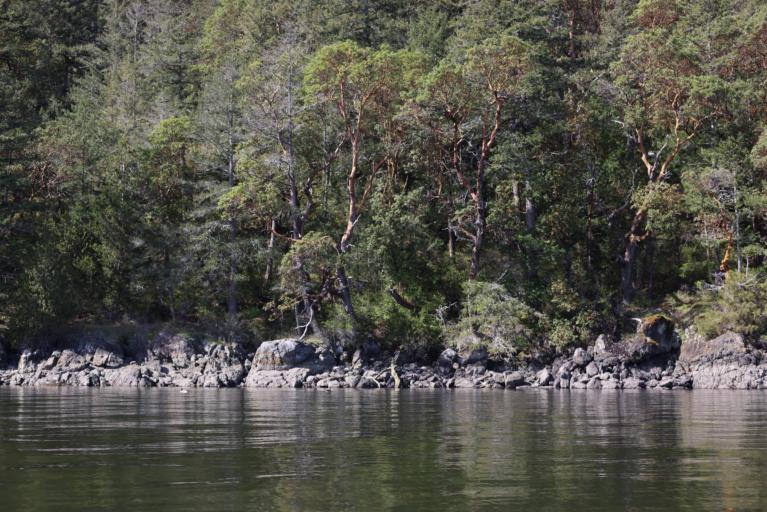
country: CA
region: British Columbia
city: Langford
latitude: 48.5702
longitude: -123.5140
